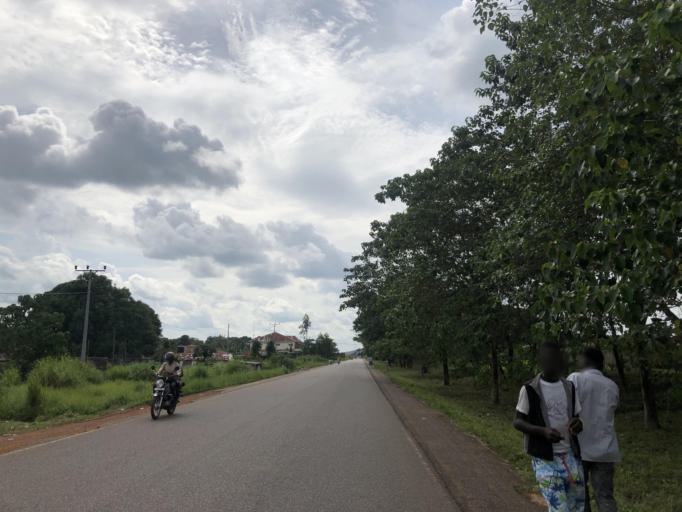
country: SL
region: Northern Province
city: Magburaka
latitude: 8.7165
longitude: -11.9295
